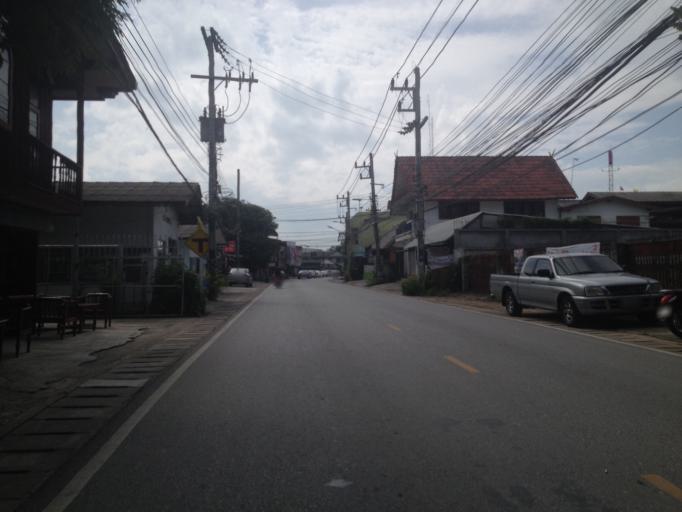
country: TH
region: Chiang Mai
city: Hang Dong
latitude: 18.6881
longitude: 98.9218
